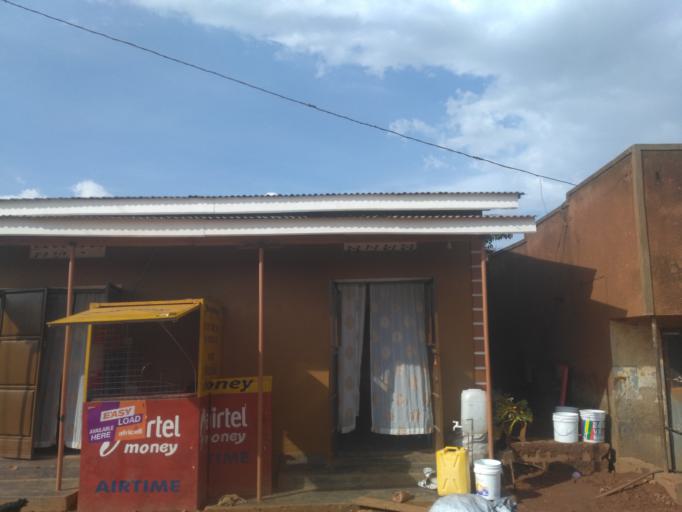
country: UG
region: Central Region
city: Kampala Central Division
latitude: 0.3617
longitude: 32.5728
